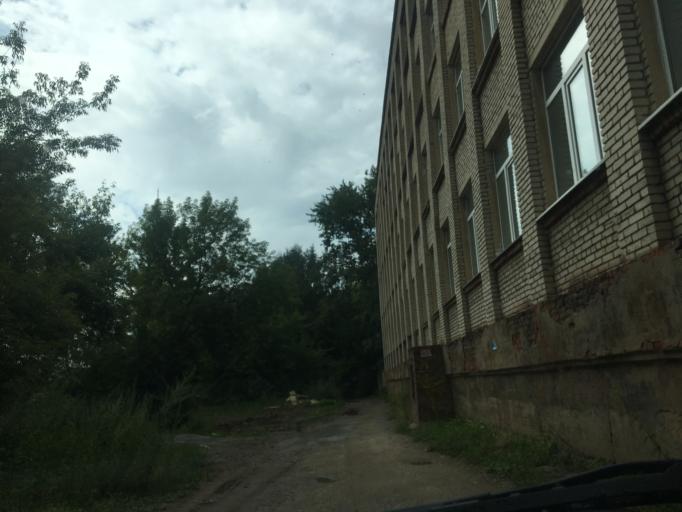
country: RU
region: Tula
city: Mendeleyevskiy
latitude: 54.1511
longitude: 37.5894
